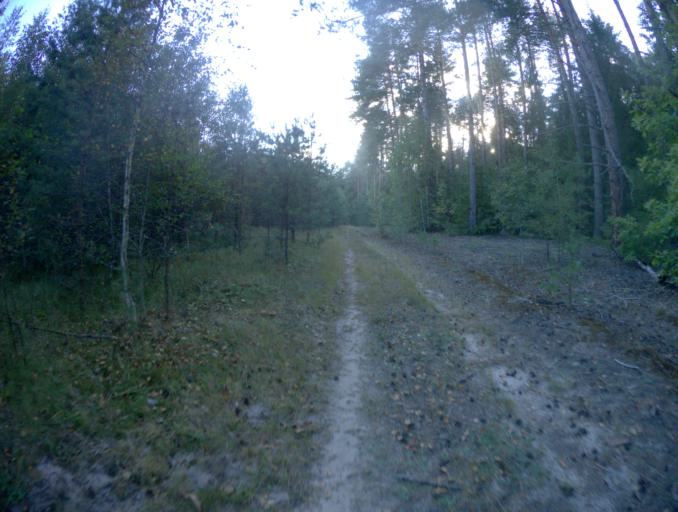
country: RU
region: Vladimir
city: Krasnaya Gorbatka
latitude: 55.7979
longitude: 41.6350
